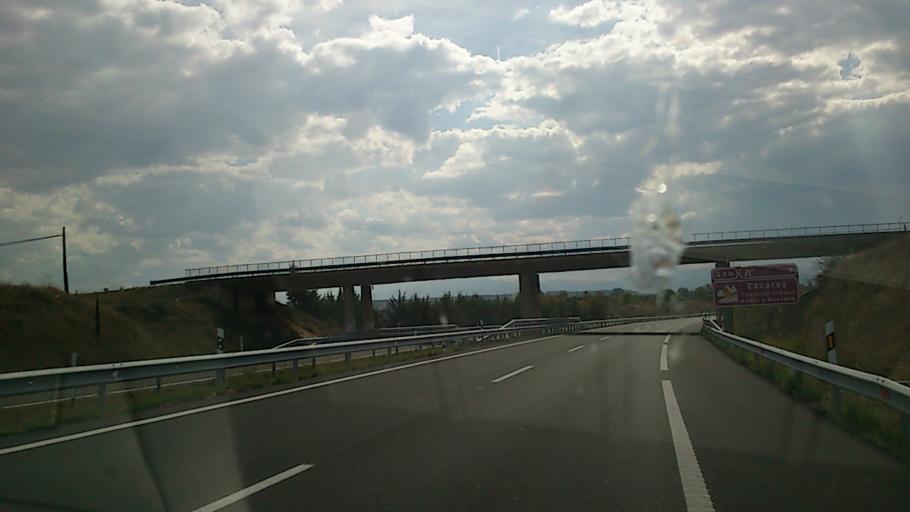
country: ES
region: La Rioja
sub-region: Provincia de La Rioja
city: Haro
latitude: 42.5858
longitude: -2.8675
